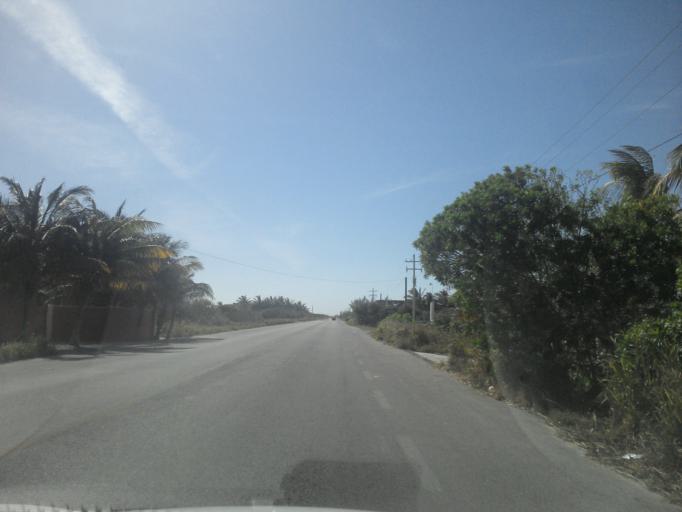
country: MX
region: Yucatan
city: Telchac Puerto
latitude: 21.3268
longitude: -89.4083
